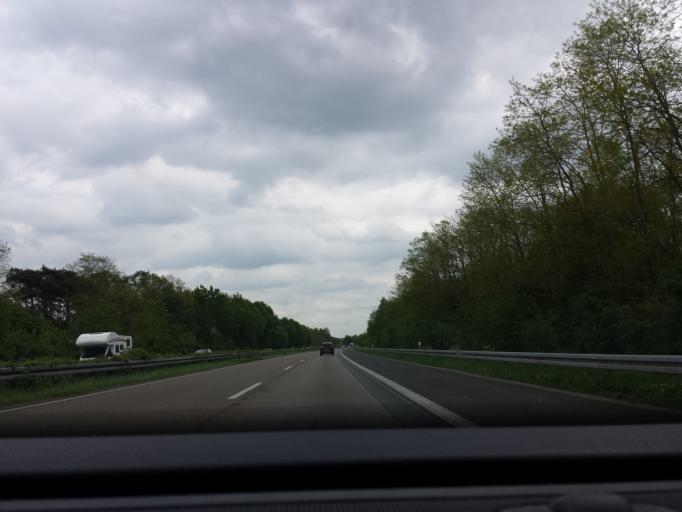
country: DE
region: North Rhine-Westphalia
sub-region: Regierungsbezirk Munster
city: Isselburg
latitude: 51.8213
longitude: 6.4218
